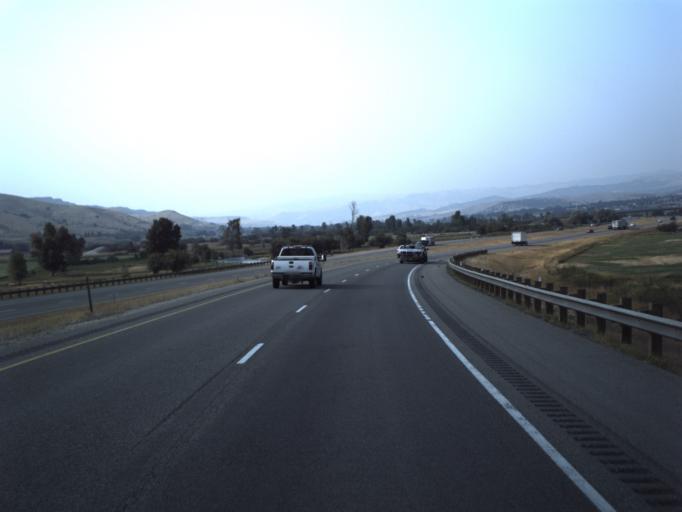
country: US
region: Utah
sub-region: Summit County
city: Coalville
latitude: 40.8492
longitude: -111.3892
